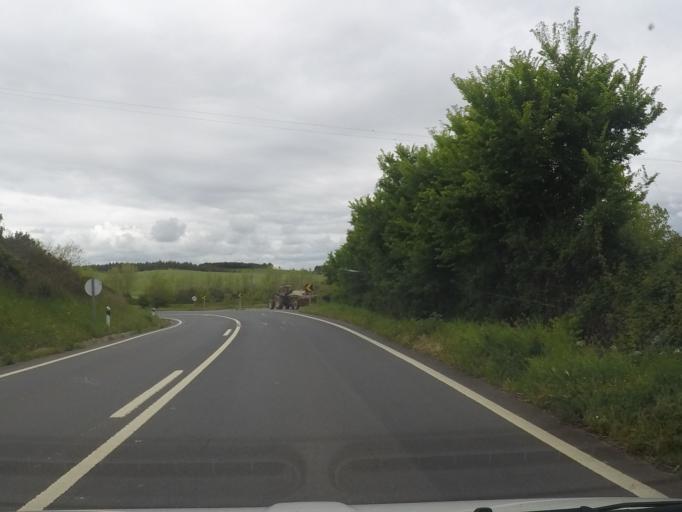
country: PT
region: Setubal
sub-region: Santiago do Cacem
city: Cercal
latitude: 37.8182
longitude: -8.6833
